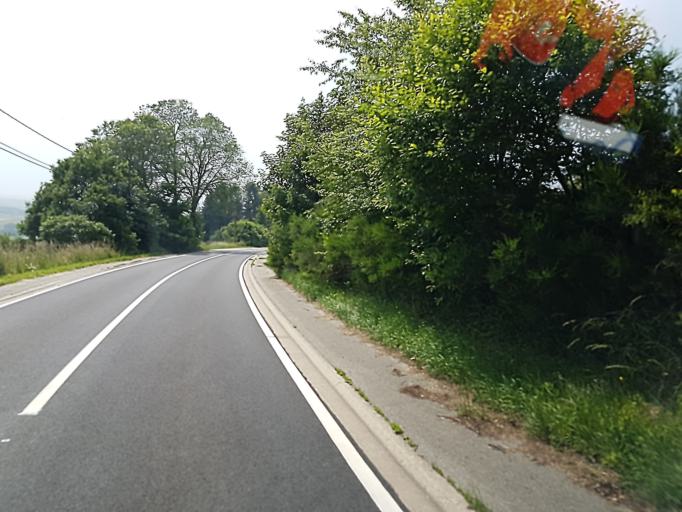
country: BE
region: Wallonia
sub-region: Province de Liege
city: Lierneux
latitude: 50.3299
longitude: 5.7704
